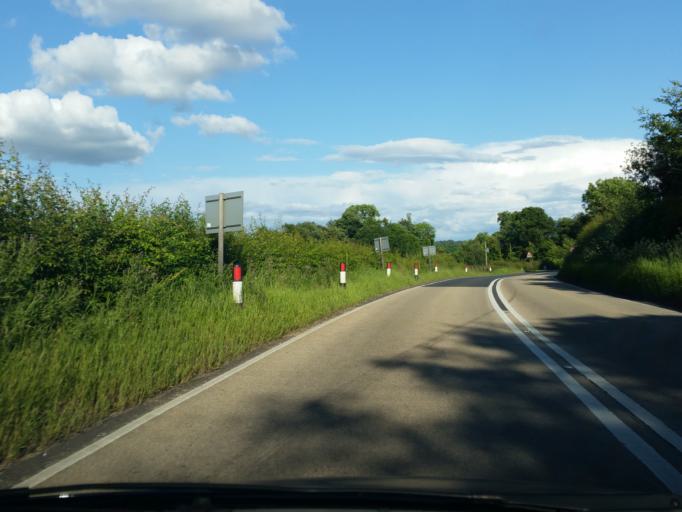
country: GB
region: Scotland
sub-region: North Lanarkshire
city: Overtown
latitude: 55.7480
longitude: -3.9398
